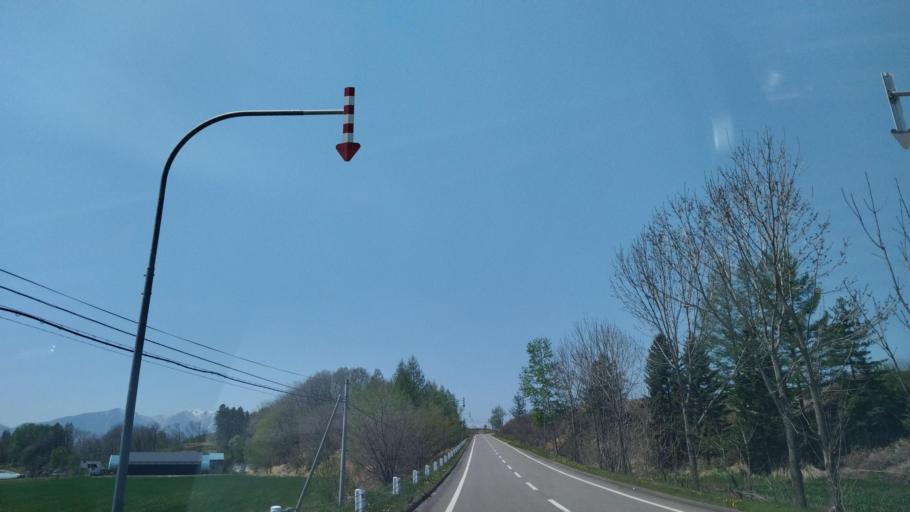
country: JP
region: Hokkaido
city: Obihiro
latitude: 42.9033
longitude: 143.0070
